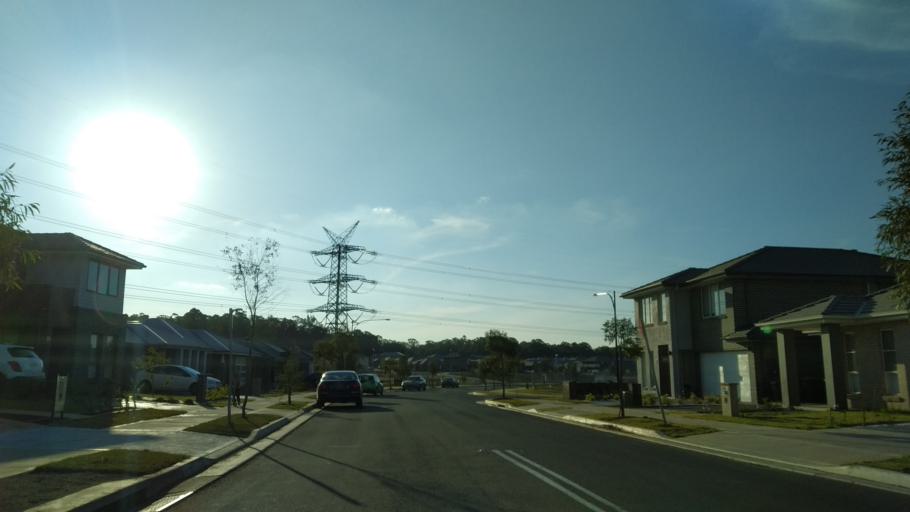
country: AU
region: New South Wales
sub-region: Penrith Municipality
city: Werrington County
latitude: -33.7373
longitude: 150.7514
